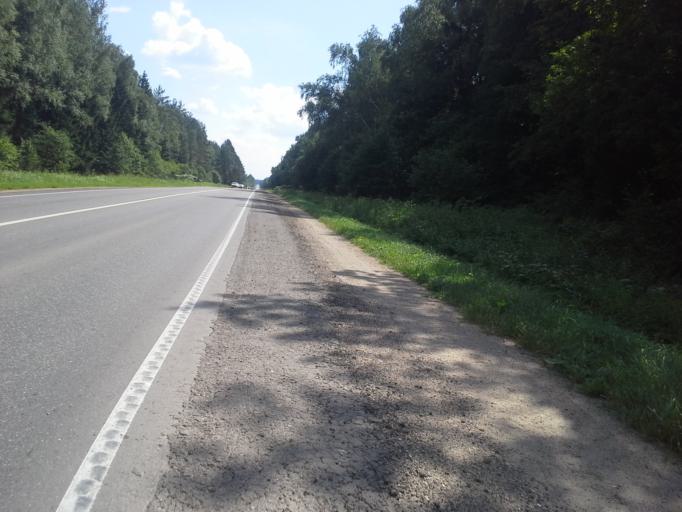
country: RU
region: Moskovskaya
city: Naro-Fominsk
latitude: 55.4608
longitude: 36.6886
